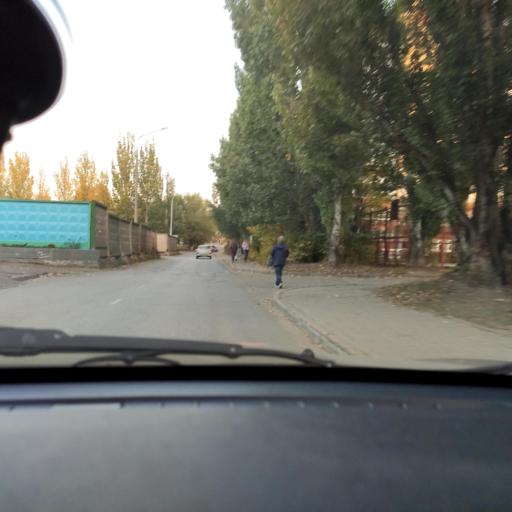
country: RU
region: Samara
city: Tol'yatti
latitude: 53.5327
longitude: 49.2910
